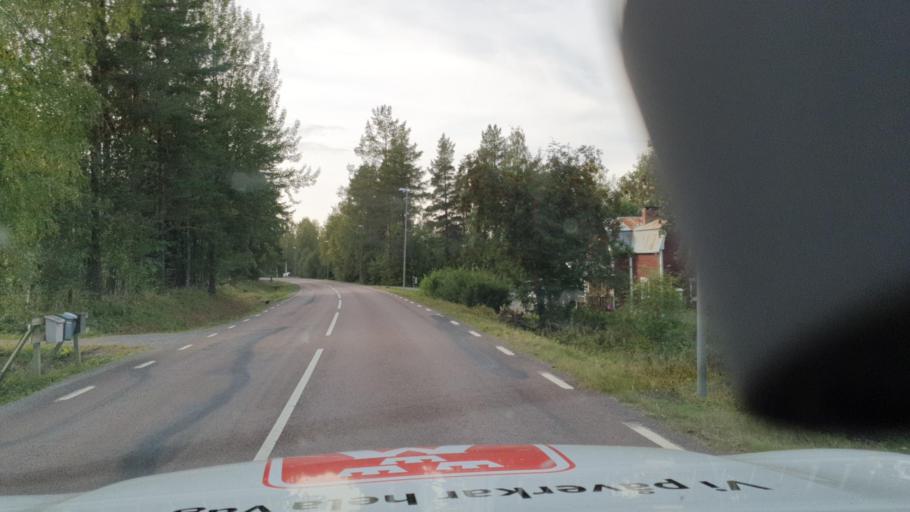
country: SE
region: Jaemtland
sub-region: Stroemsunds Kommun
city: Stroemsund
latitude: 63.8071
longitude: 15.6878
